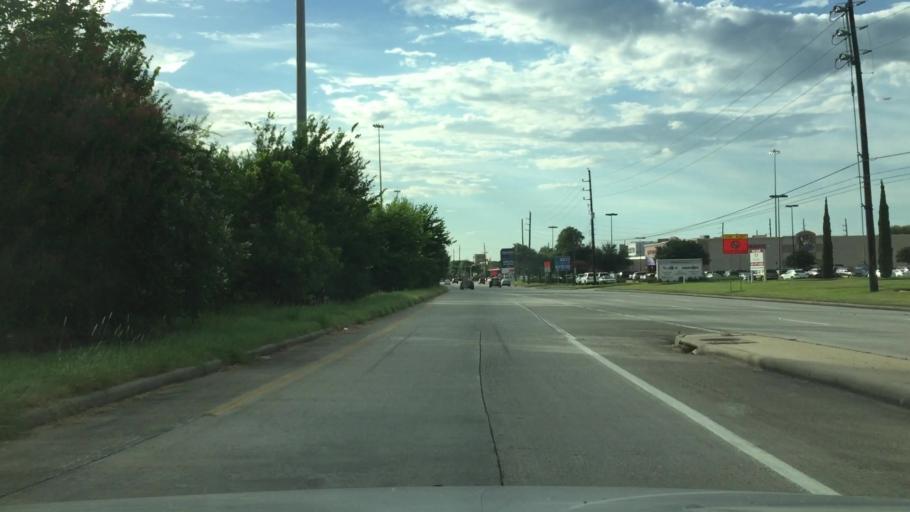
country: US
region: Texas
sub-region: Harris County
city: Hudson
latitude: 29.9588
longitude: -95.5446
